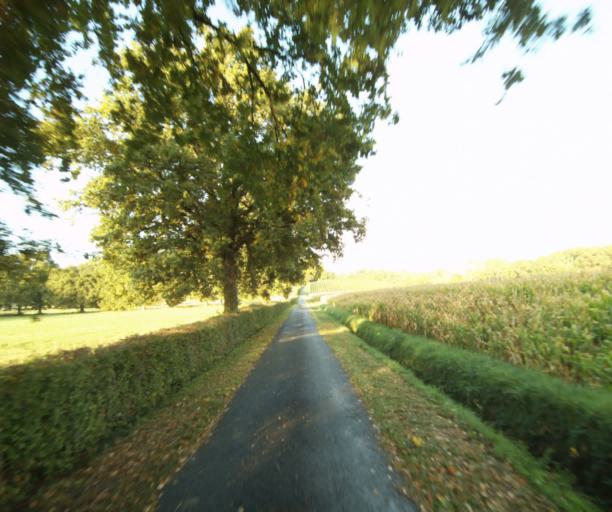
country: FR
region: Midi-Pyrenees
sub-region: Departement du Gers
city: Cazaubon
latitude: 43.9015
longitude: -0.0382
